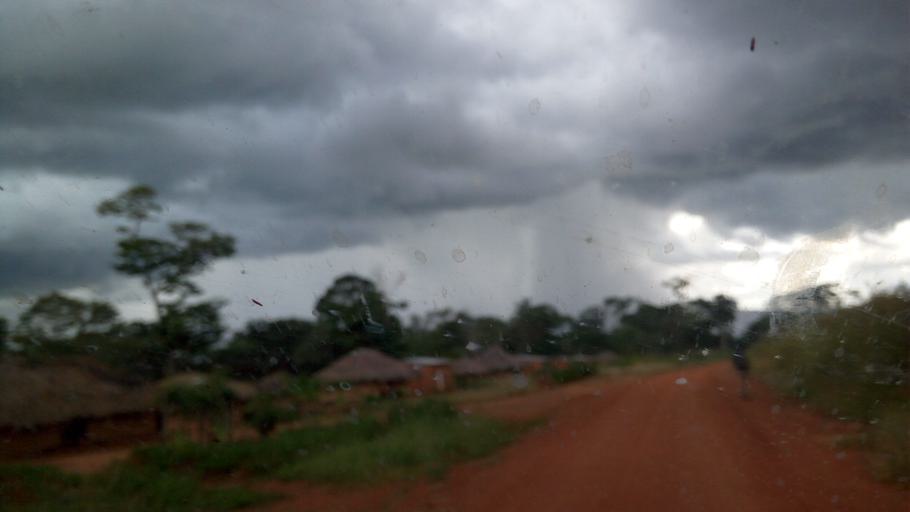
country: ZM
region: Northern
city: Kaputa
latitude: -8.0794
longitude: 29.1635
